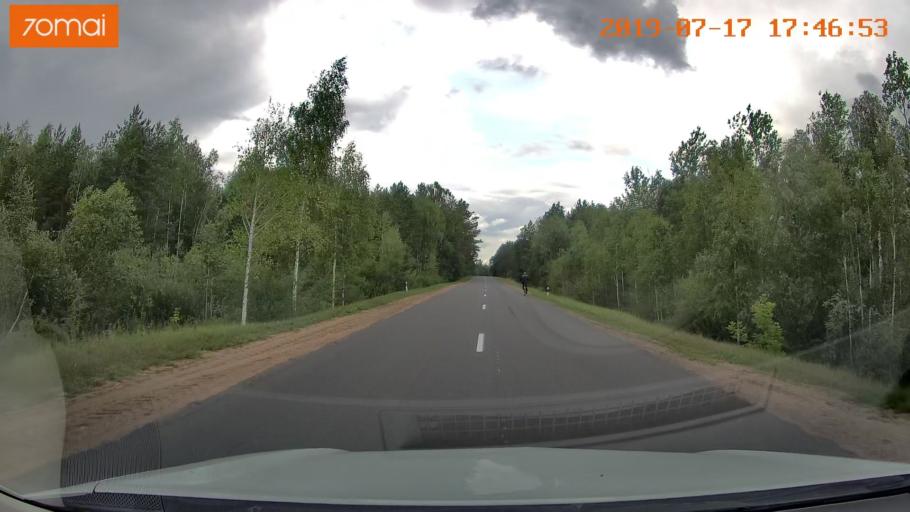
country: BY
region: Mogilev
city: Hlusha
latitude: 53.1033
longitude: 28.8336
